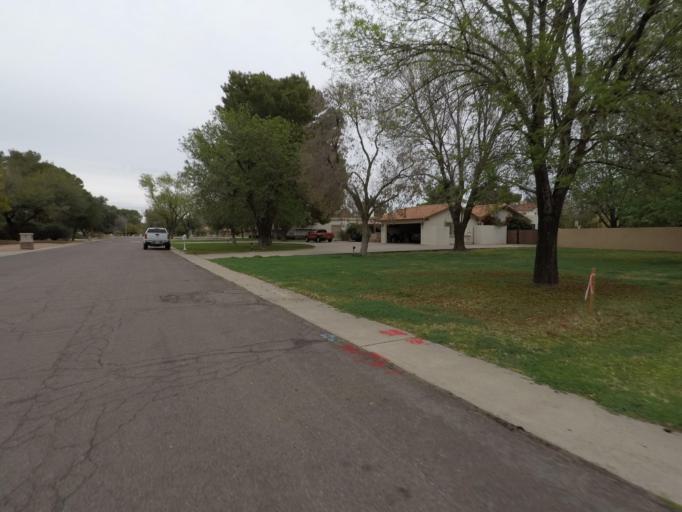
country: US
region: Arizona
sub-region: Maricopa County
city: Guadalupe
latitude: 33.3359
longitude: -111.9209
